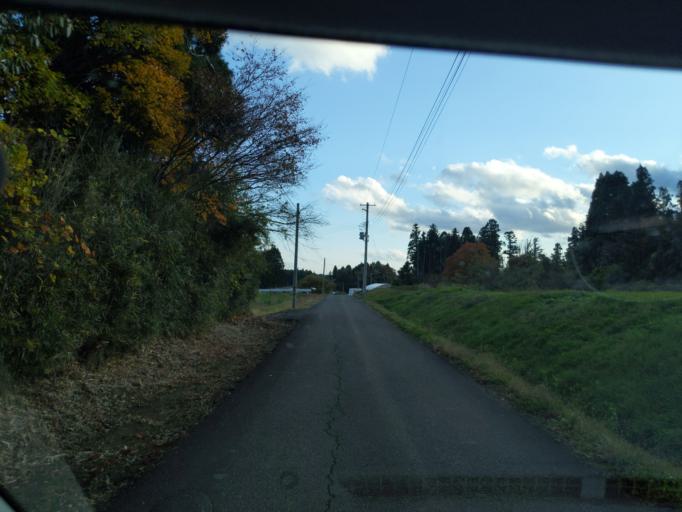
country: JP
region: Iwate
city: Mizusawa
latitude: 39.1077
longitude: 141.0394
